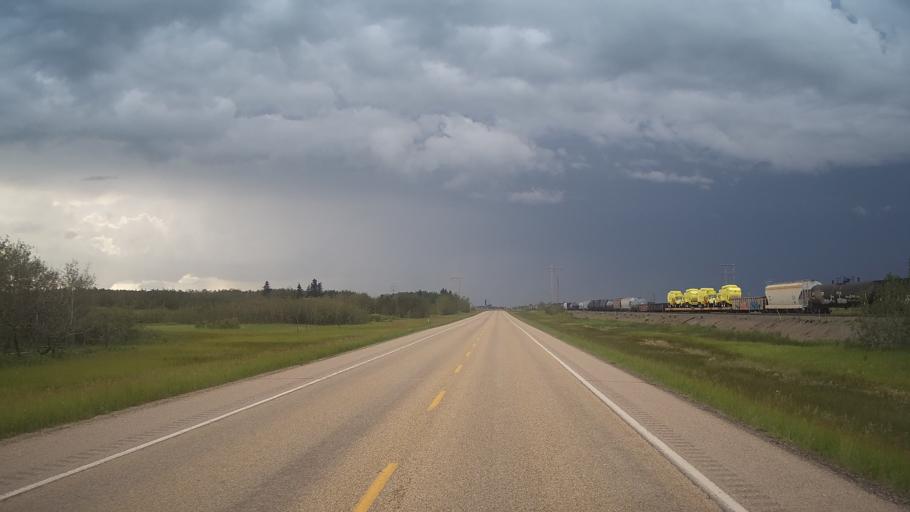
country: CA
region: Alberta
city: Tofield
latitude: 53.2780
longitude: -112.3974
